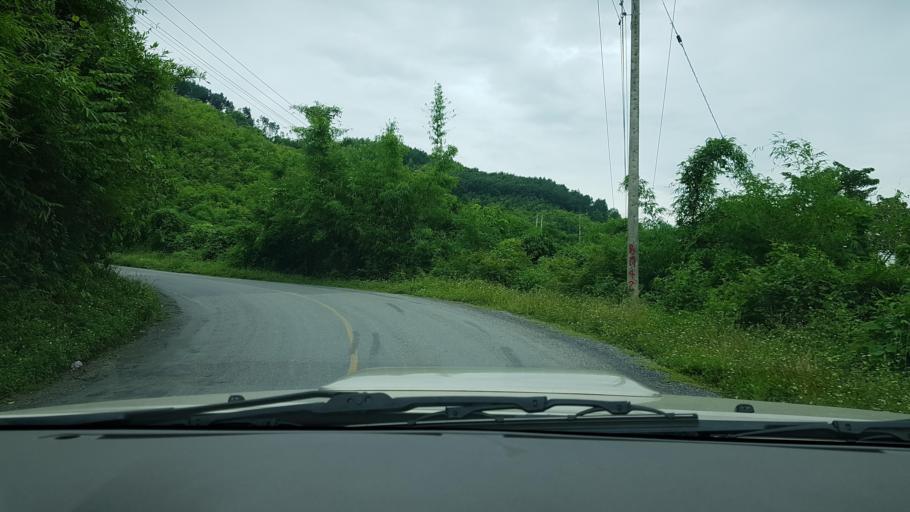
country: LA
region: Loungnamtha
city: Muang Nale
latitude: 20.1675
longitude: 101.5092
